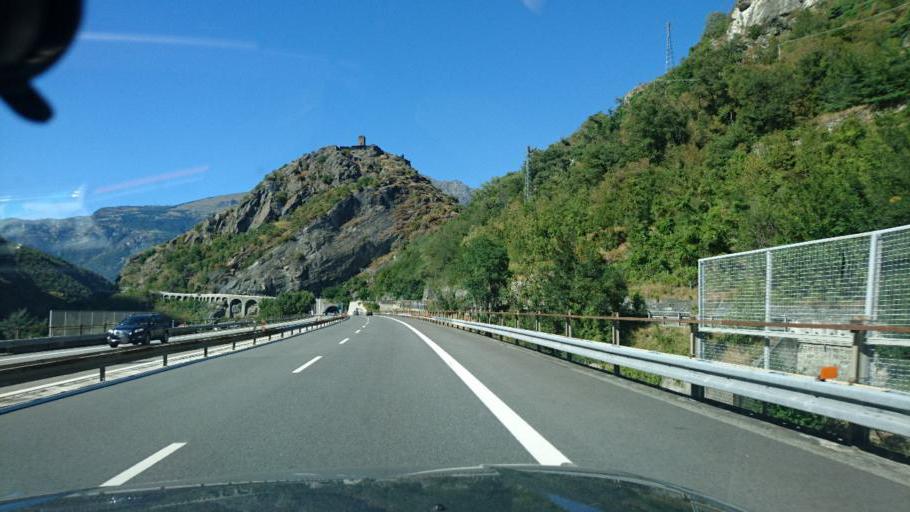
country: IT
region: Aosta Valley
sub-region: Valle d'Aosta
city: Montjovet
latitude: 45.7175
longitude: 7.6706
